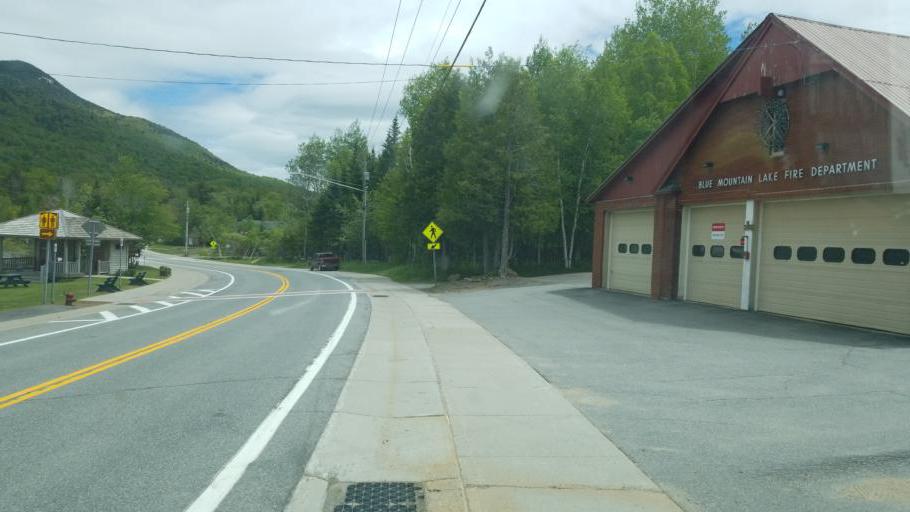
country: US
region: New York
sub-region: Franklin County
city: Tupper Lake
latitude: 43.8544
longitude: -74.4353
